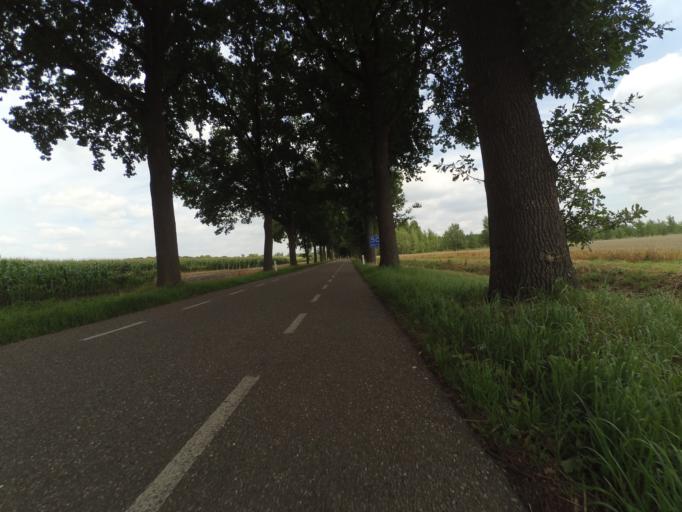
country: NL
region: Limburg
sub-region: Gemeente Sittard-Geleen
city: Limbricht
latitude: 51.0175
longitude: 5.8426
